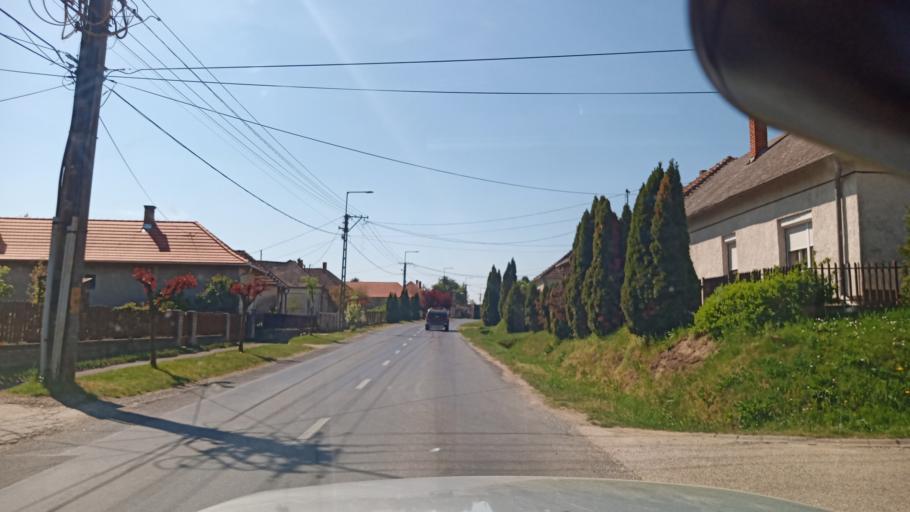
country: HU
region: Zala
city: Sarmellek
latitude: 46.7455
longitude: 17.1071
